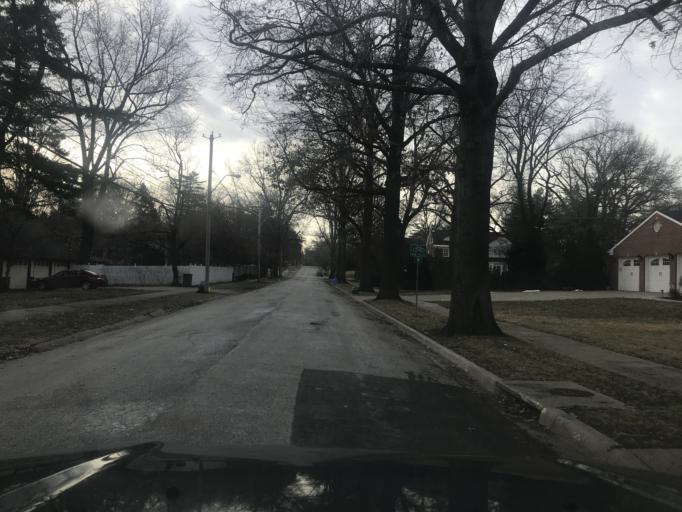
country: US
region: Kansas
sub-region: Johnson County
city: Mission Hills
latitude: 39.0280
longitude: -94.5996
